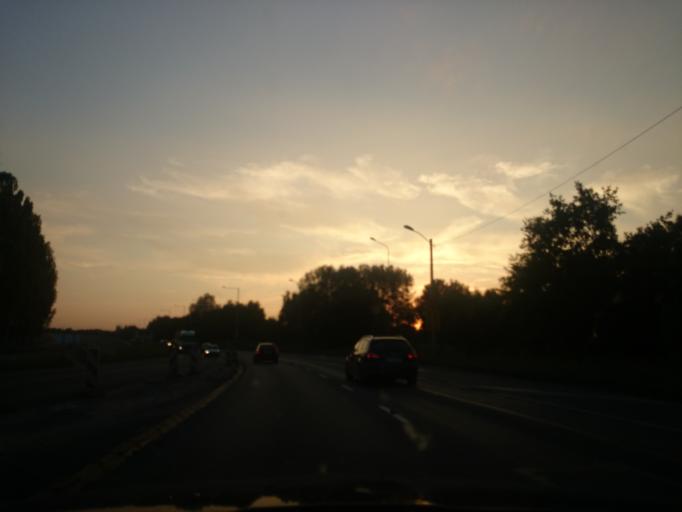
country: PL
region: West Pomeranian Voivodeship
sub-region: Szczecin
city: Szczecin
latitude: 53.3869
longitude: 14.6396
